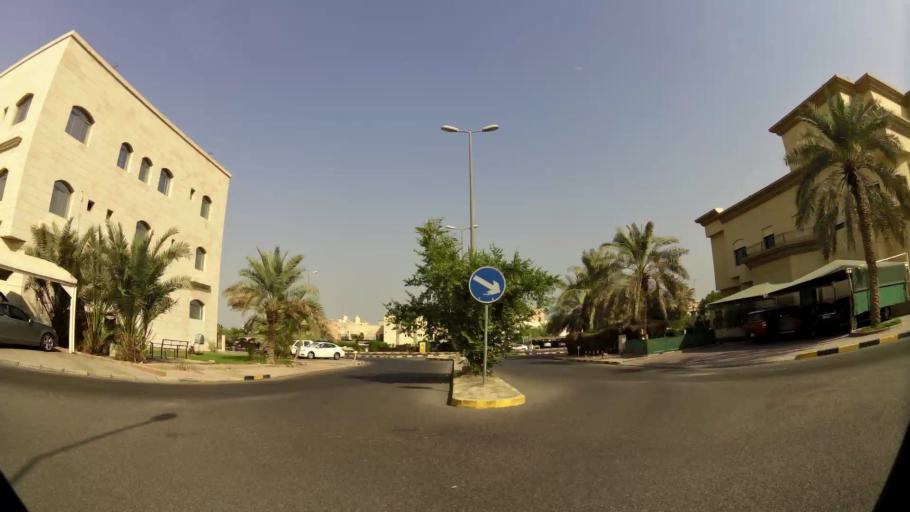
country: KW
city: Bayan
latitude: 29.2874
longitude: 48.0503
